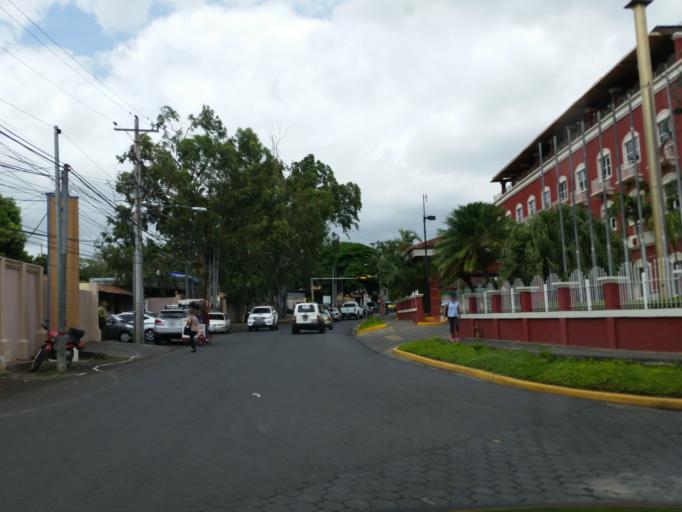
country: NI
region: Managua
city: Managua
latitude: 12.1241
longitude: -86.2661
